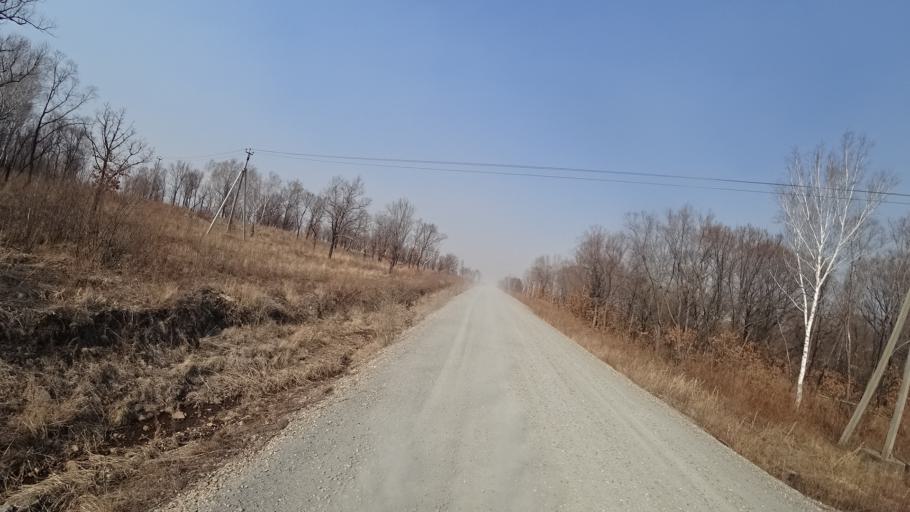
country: RU
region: Amur
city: Novobureyskiy
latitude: 49.8004
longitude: 129.9595
